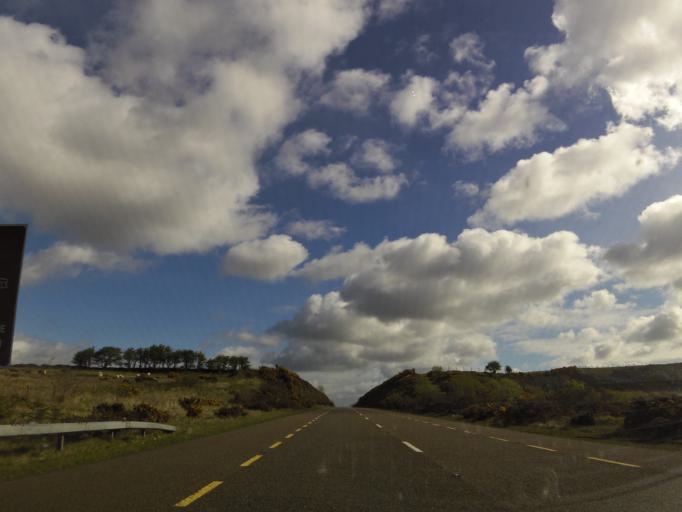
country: IE
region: Connaught
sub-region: Maigh Eo
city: Kiltamagh
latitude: 53.7880
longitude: -8.9372
